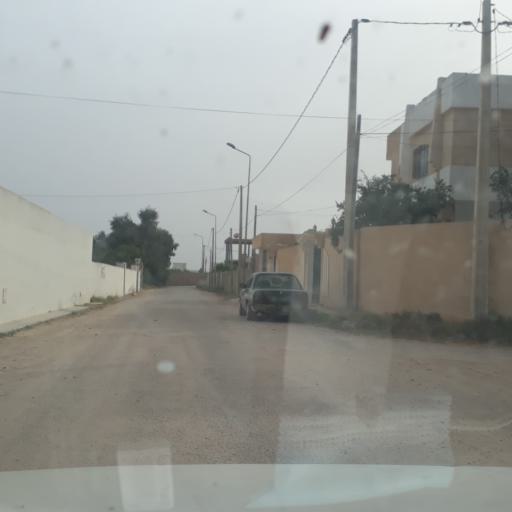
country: TN
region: Safaqis
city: Al Qarmadah
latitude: 34.8218
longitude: 10.7760
